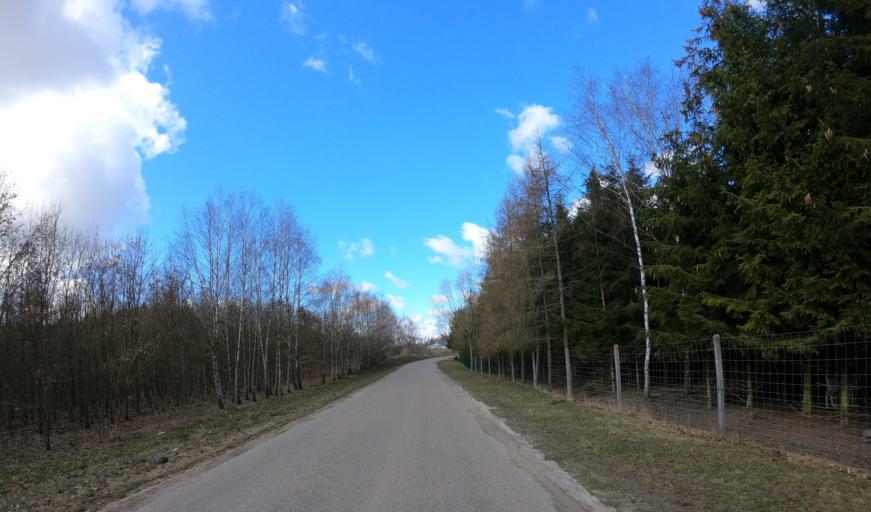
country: PL
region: West Pomeranian Voivodeship
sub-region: Powiat drawski
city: Zlocieniec
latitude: 53.4831
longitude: 15.9140
